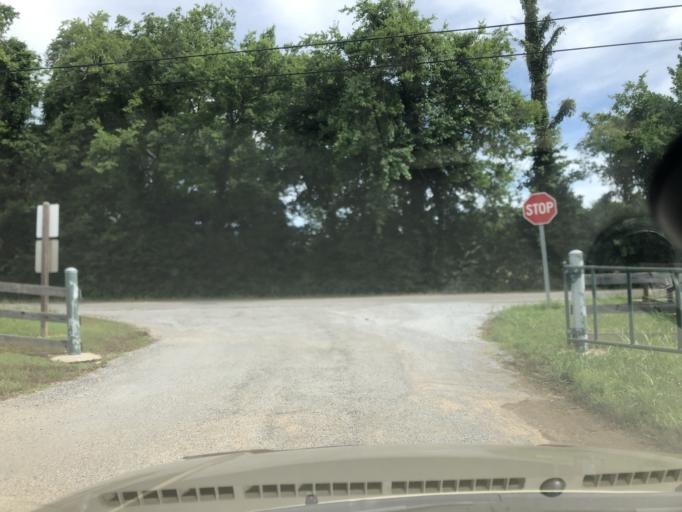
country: US
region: Tennessee
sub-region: Davidson County
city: Lakewood
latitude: 36.2168
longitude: -86.6471
